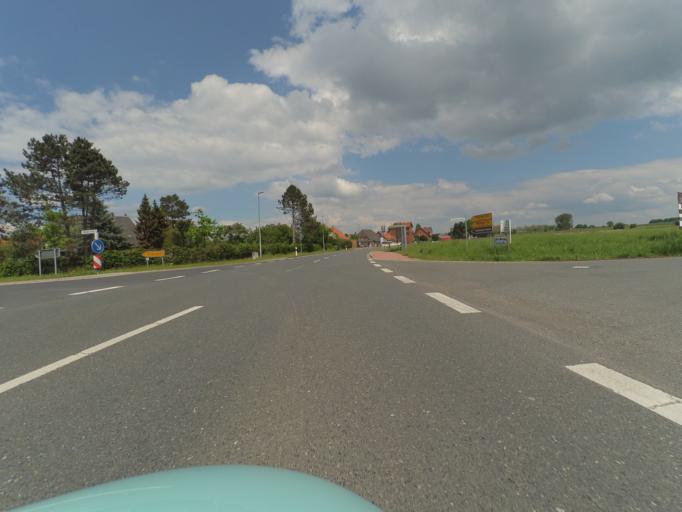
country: DE
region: Lower Saxony
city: Sehnde
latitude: 52.2929
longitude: 9.9099
